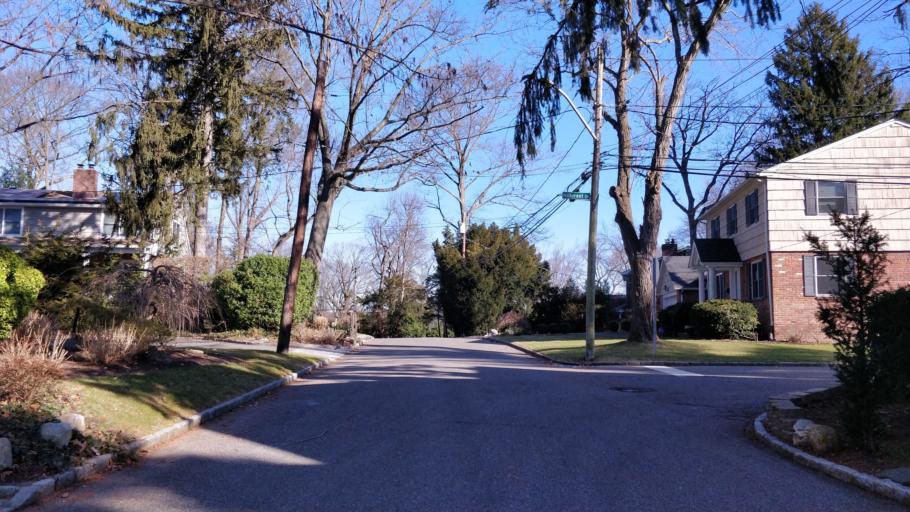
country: US
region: New York
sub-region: Nassau County
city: Glen Head
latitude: 40.8402
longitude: -73.6188
